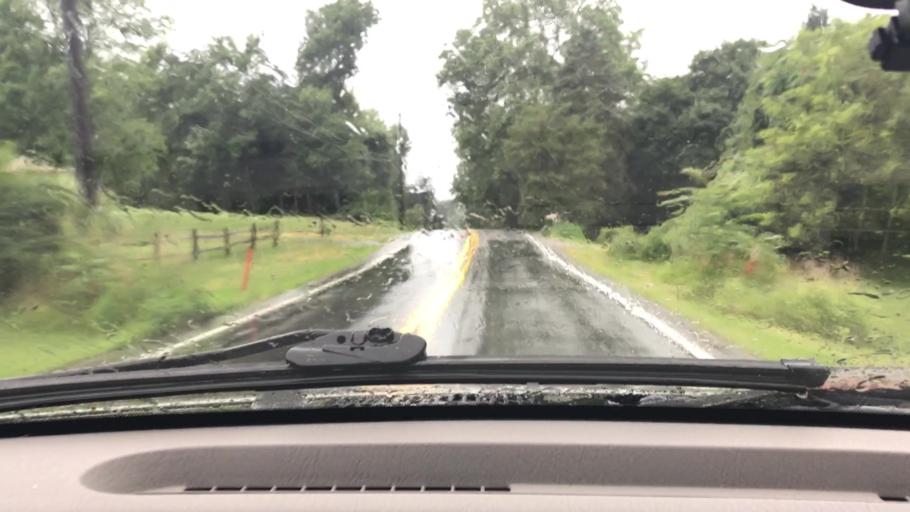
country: US
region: Pennsylvania
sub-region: Lancaster County
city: Elizabethtown
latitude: 40.1433
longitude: -76.6501
